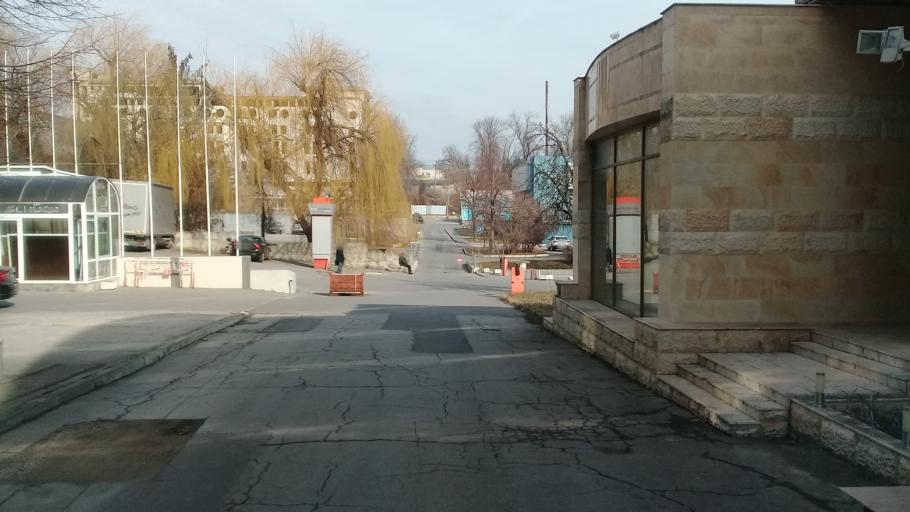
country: MD
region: Chisinau
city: Chisinau
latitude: 47.0168
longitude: 28.8011
